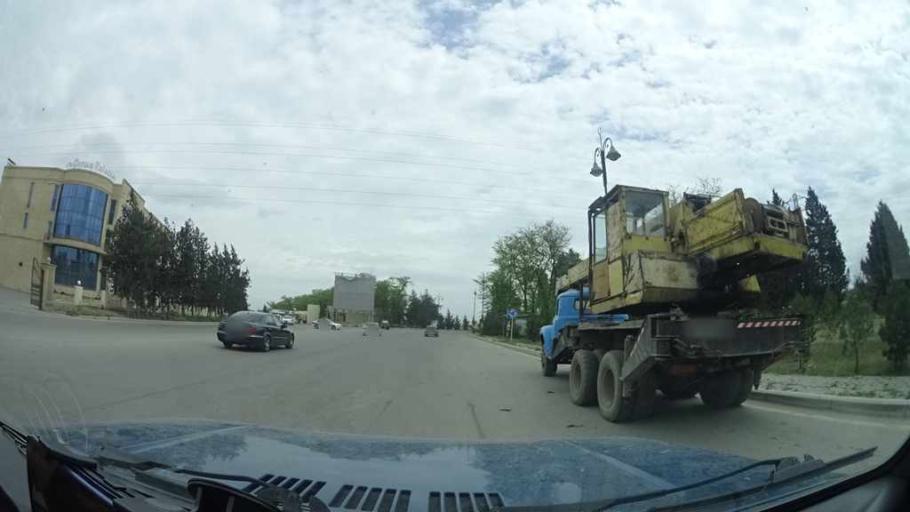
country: AZ
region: Samux
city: Samux
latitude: 40.7245
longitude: 46.3983
